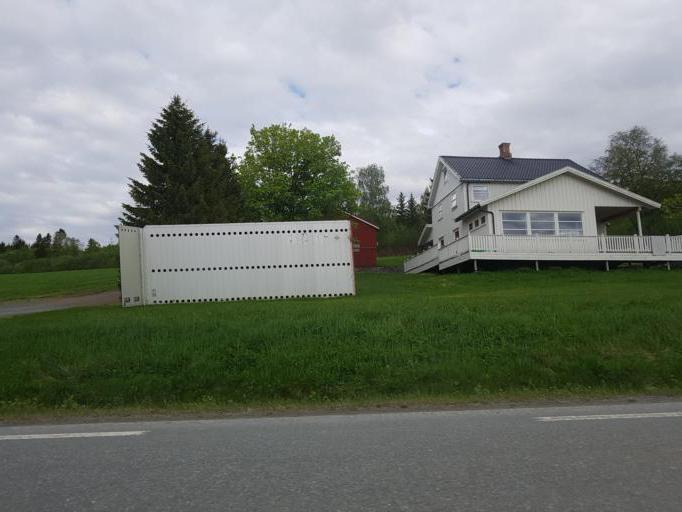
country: NO
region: Nord-Trondelag
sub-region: Levanger
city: Skogn
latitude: 63.6914
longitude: 11.2255
